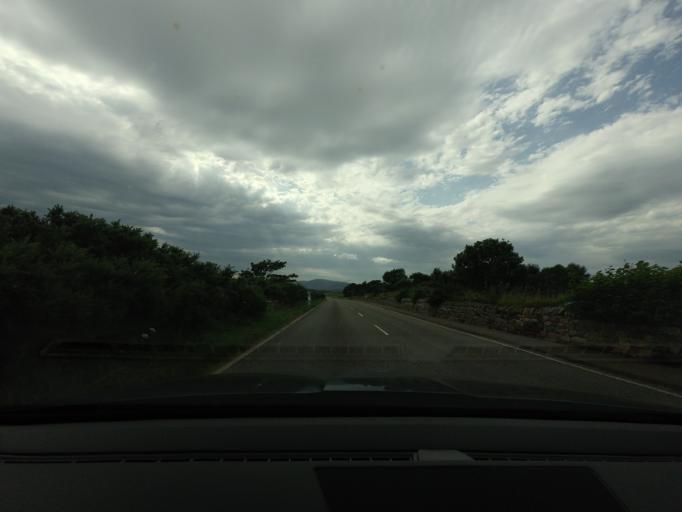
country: GB
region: Scotland
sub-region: Highland
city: Invergordon
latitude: 57.6915
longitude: -4.1920
